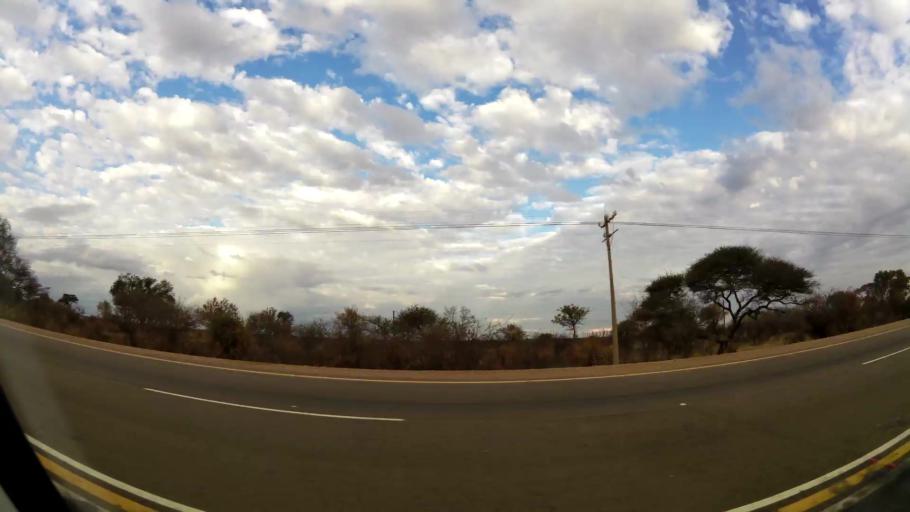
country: ZA
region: Limpopo
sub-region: Waterberg District Municipality
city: Modimolle
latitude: -24.5047
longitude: 28.7292
